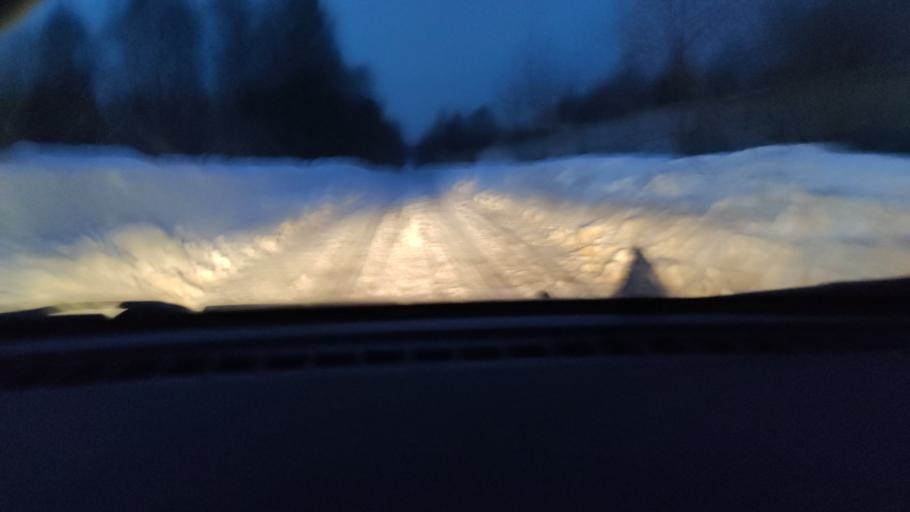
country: RU
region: Perm
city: Kondratovo
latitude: 58.0658
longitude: 56.1262
